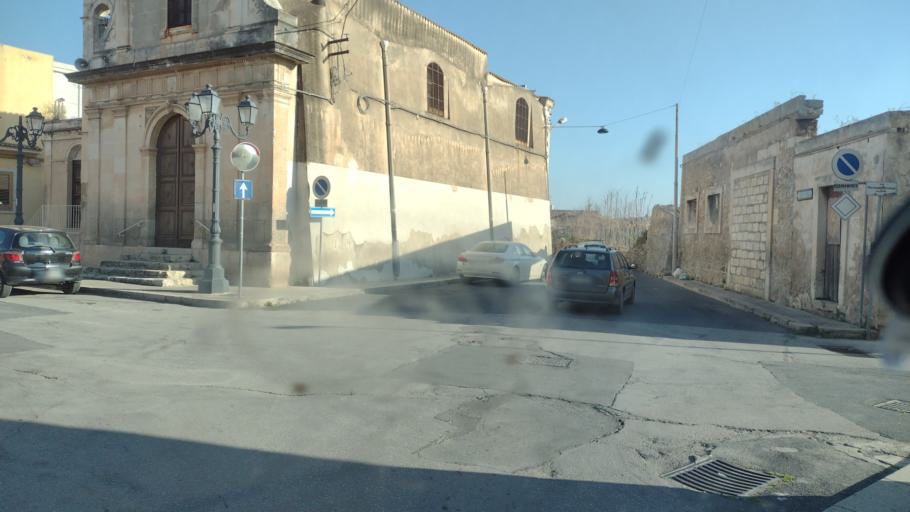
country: IT
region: Sicily
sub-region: Provincia di Siracusa
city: Avola
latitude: 36.9053
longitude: 15.1369
